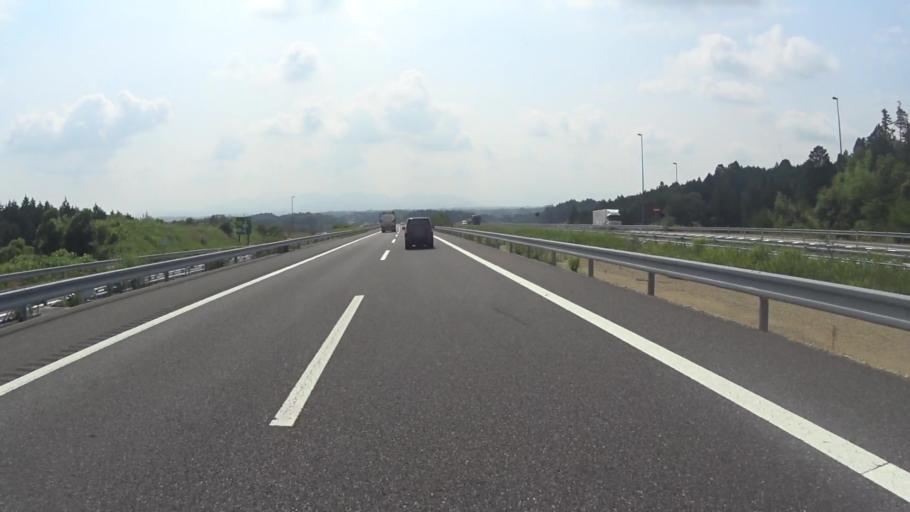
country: JP
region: Shiga Prefecture
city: Minakuchicho-matoba
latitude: 34.9167
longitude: 136.1478
